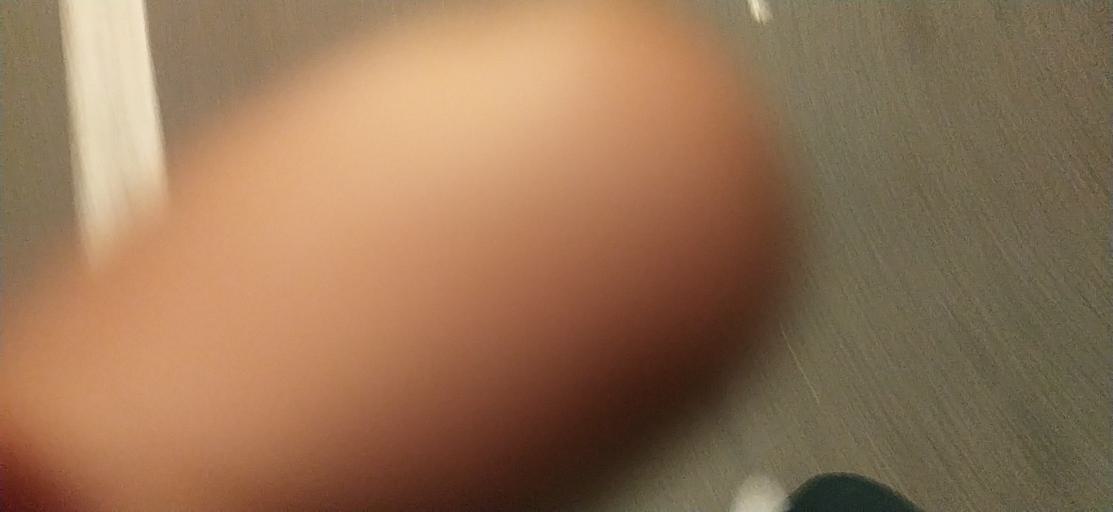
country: IN
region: Uttar Pradesh
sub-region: Ghaziabad
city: Loni
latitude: 28.7016
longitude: 77.2822
